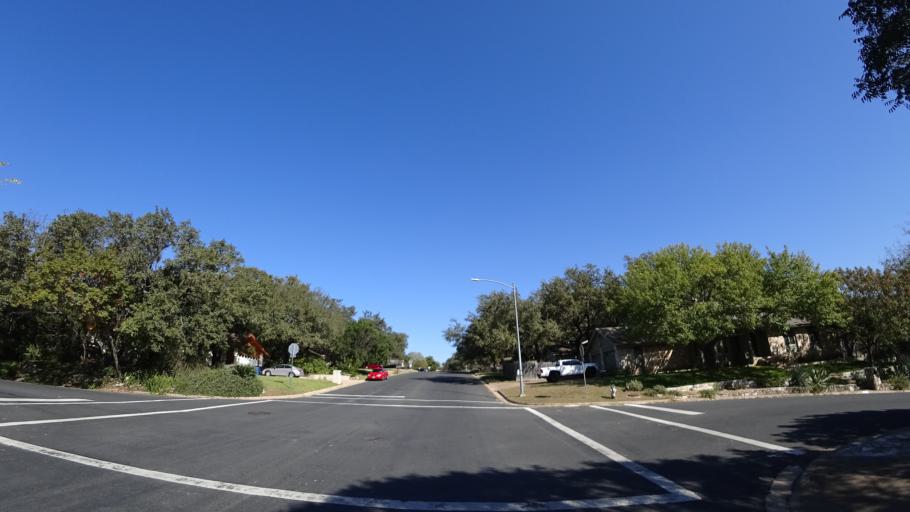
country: US
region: Texas
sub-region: Williamson County
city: Jollyville
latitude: 30.4219
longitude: -97.7659
